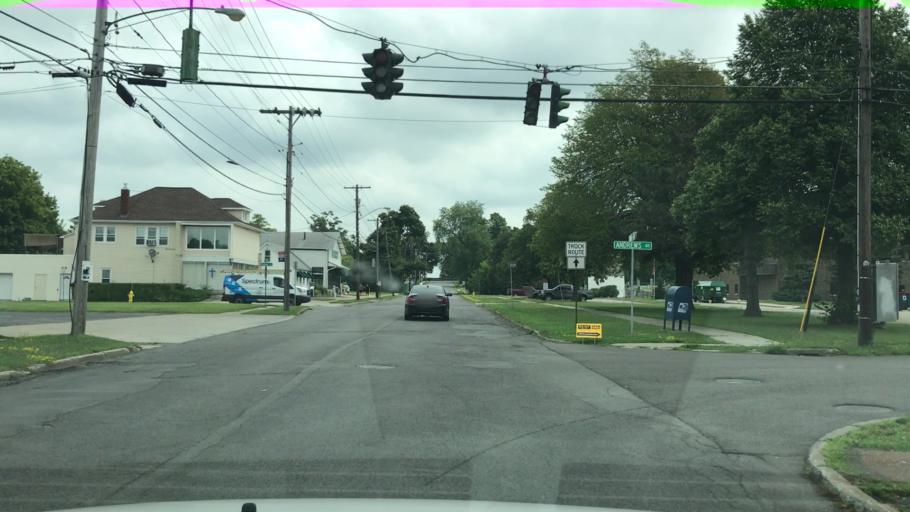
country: US
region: New York
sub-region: Erie County
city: Sloan
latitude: 42.9228
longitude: -78.7965
